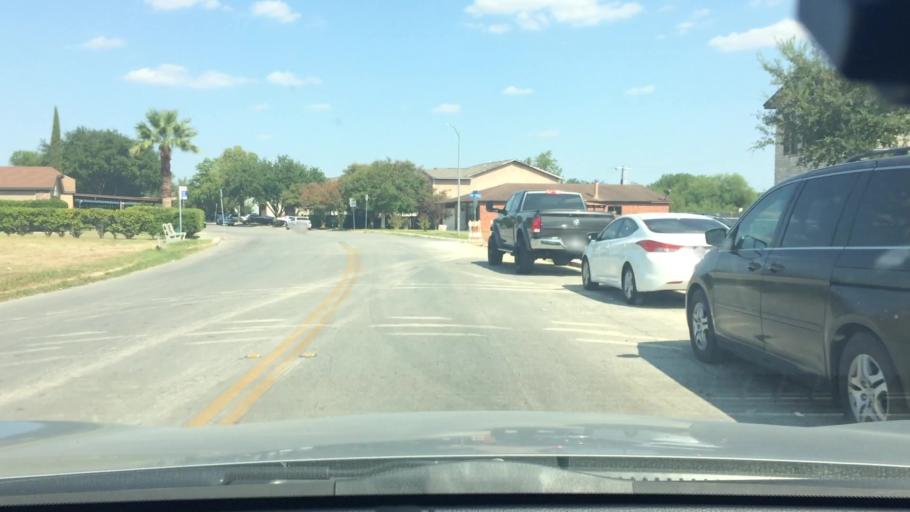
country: US
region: Texas
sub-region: Bexar County
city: Kirby
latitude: 29.4686
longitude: -98.3729
